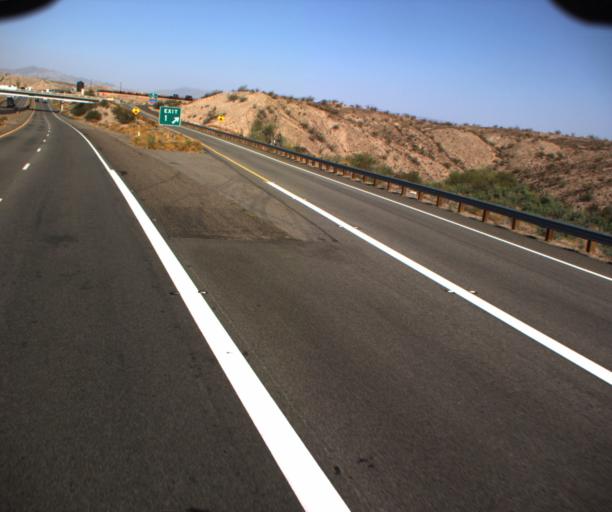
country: US
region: California
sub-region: San Bernardino County
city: Needles
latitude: 34.7184
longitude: -114.4754
